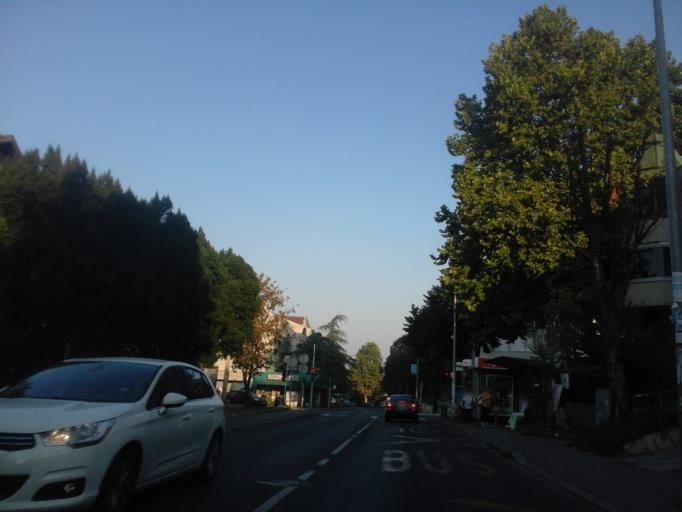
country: RS
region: Central Serbia
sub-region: Belgrade
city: Cukarica
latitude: 44.7678
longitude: 20.4208
